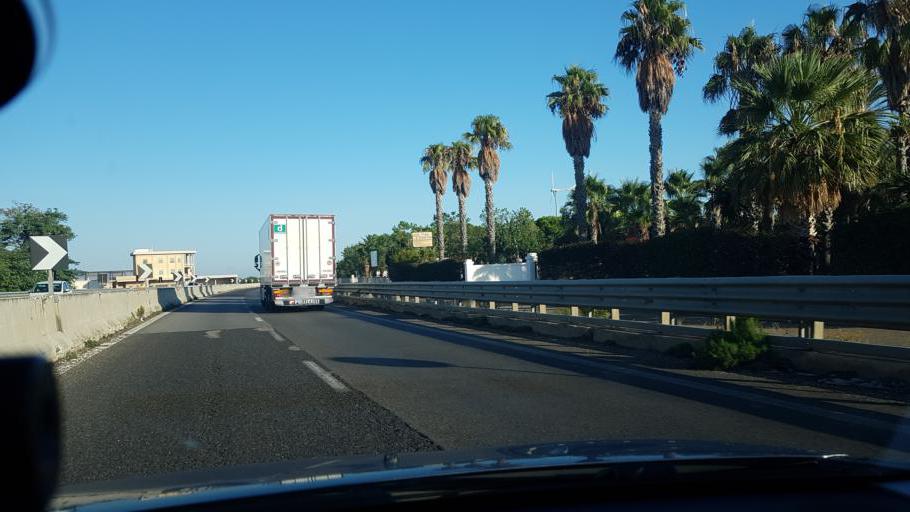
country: IT
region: Apulia
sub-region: Provincia di Brindisi
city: Fasano
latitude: 40.8576
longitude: 17.3505
